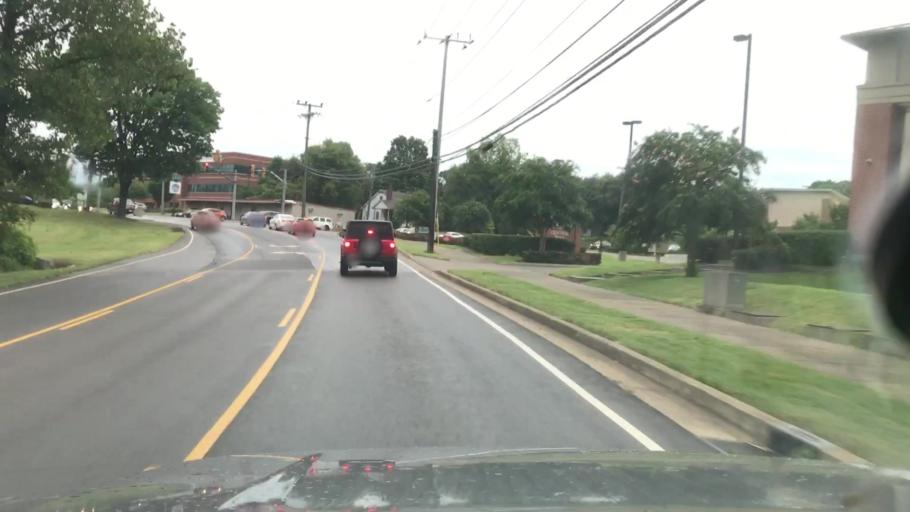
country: US
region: Tennessee
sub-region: Davidson County
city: Lakewood
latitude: 36.1752
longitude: -86.6151
